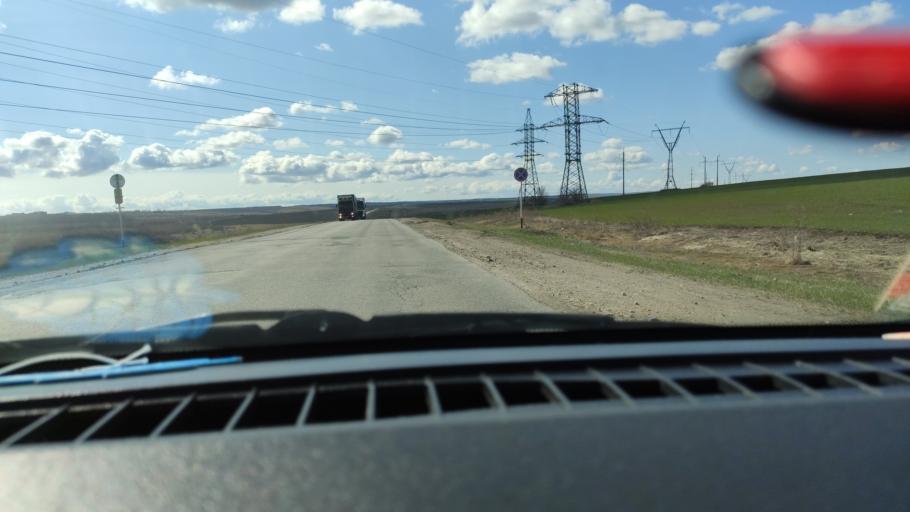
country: RU
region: Samara
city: Varlamovo
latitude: 53.0792
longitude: 48.3542
